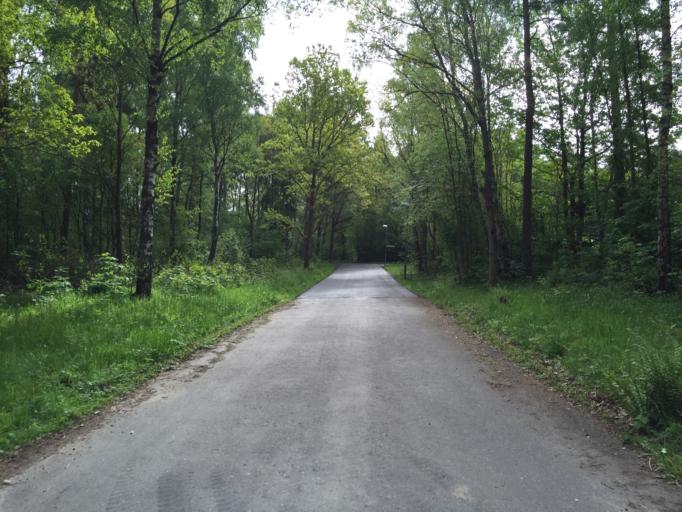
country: SE
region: Skane
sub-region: Lunds Kommun
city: Veberod
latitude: 55.6245
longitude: 13.5119
